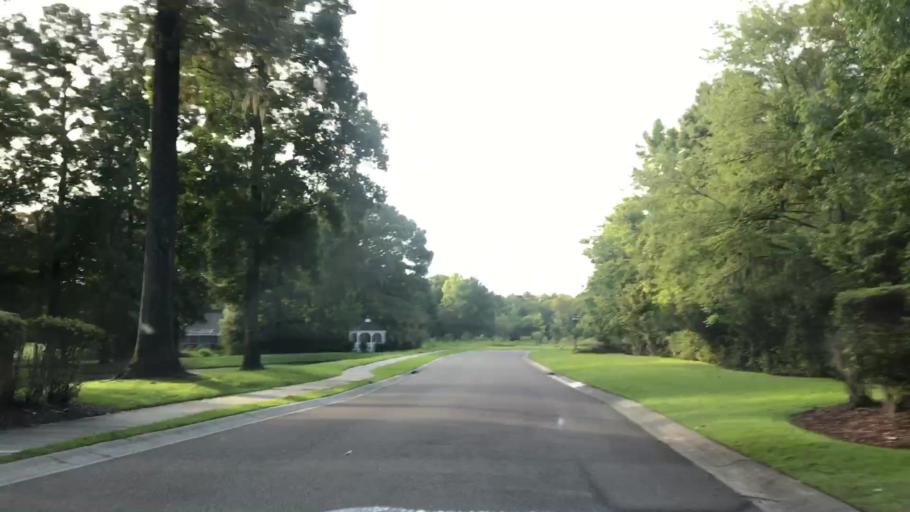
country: US
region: South Carolina
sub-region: Charleston County
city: Shell Point
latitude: 32.8356
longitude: -80.0704
